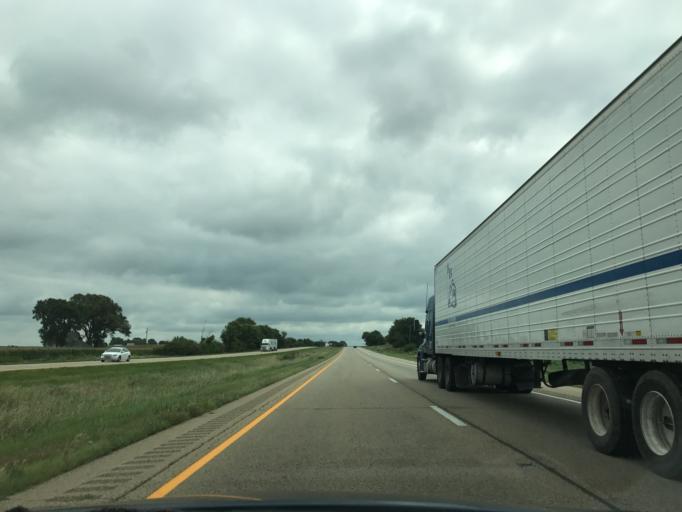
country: US
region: Illinois
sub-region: Bureau County
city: Walnut
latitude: 41.3873
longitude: -89.7453
